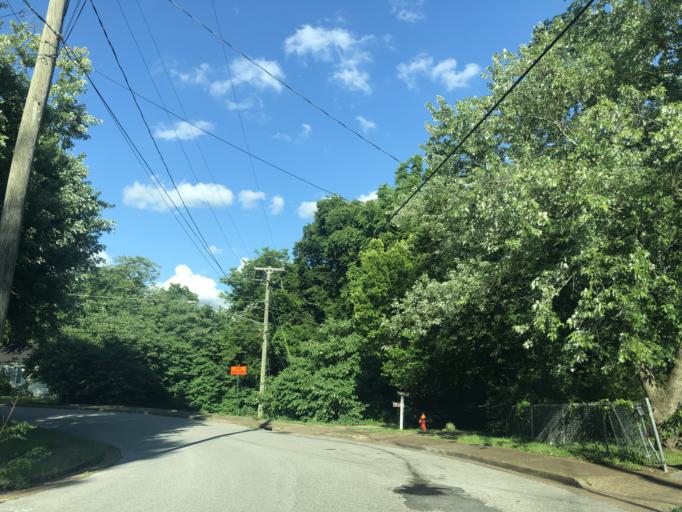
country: US
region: Tennessee
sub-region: Davidson County
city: Nashville
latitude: 36.1841
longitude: -86.7627
